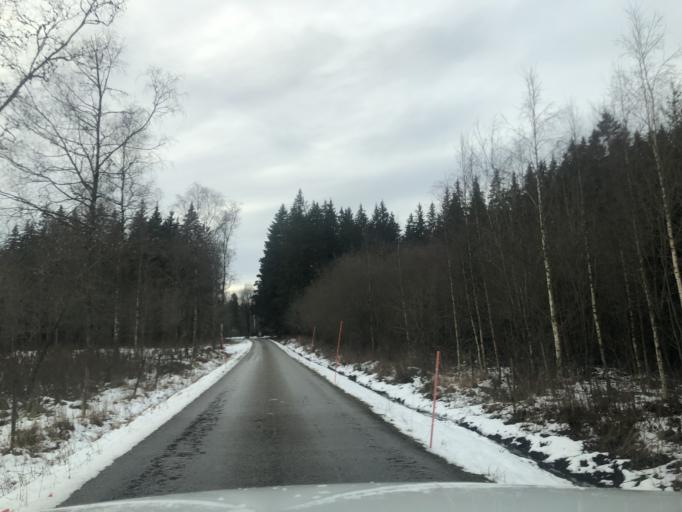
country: SE
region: Vaestra Goetaland
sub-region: Ulricehamns Kommun
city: Ulricehamn
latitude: 57.8104
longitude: 13.5162
